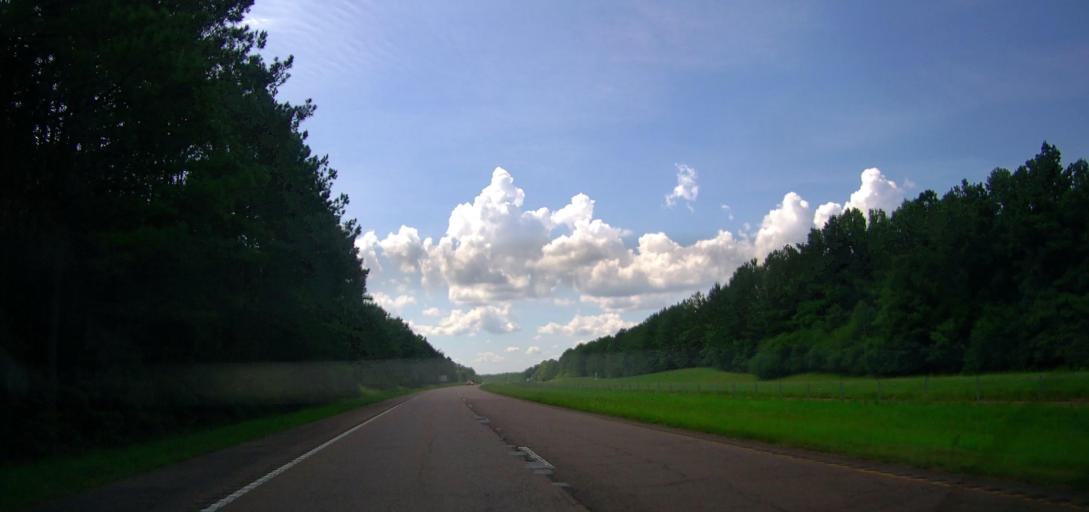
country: US
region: Mississippi
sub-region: Lowndes County
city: New Hope
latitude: 33.4995
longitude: -88.3034
